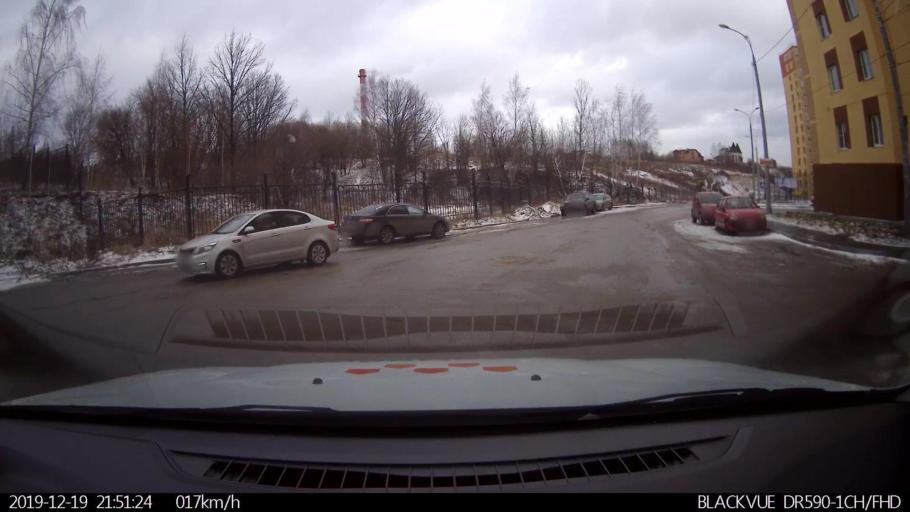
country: RU
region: Nizjnij Novgorod
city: Afonino
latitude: 56.2823
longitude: 44.0857
